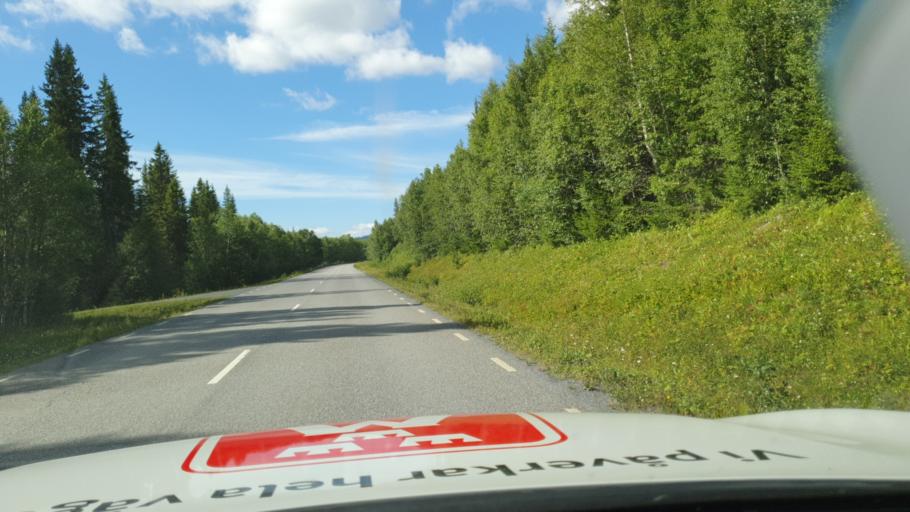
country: SE
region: Jaemtland
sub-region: Are Kommun
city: Are
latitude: 63.6840
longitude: 13.0000
